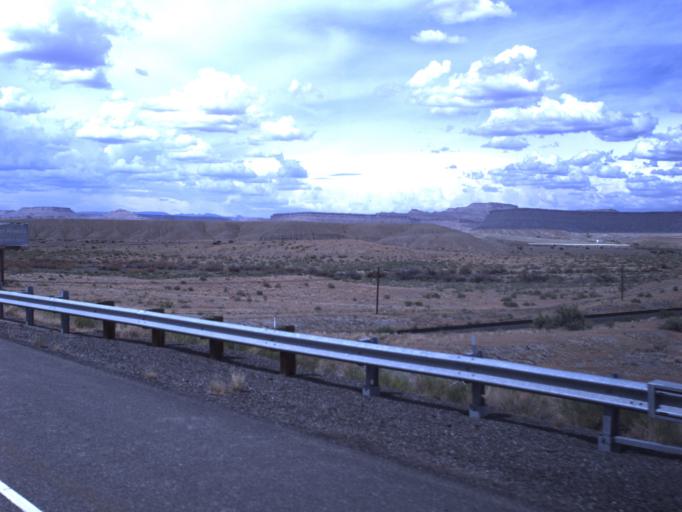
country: US
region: Utah
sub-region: Carbon County
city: East Carbon City
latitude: 38.9833
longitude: -110.1241
